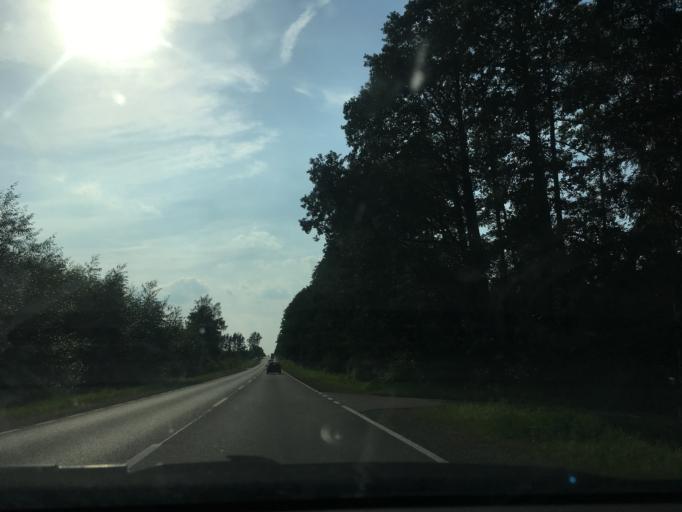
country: PL
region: Podlasie
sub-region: Powiat bialostocki
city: Suprasl
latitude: 53.1255
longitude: 23.2964
